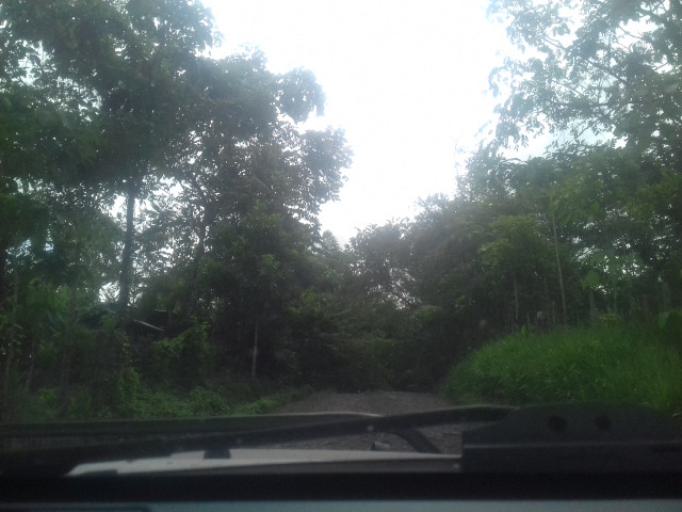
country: NI
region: Atlantico Norte (RAAN)
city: Waslala
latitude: 13.5017
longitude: -85.2333
